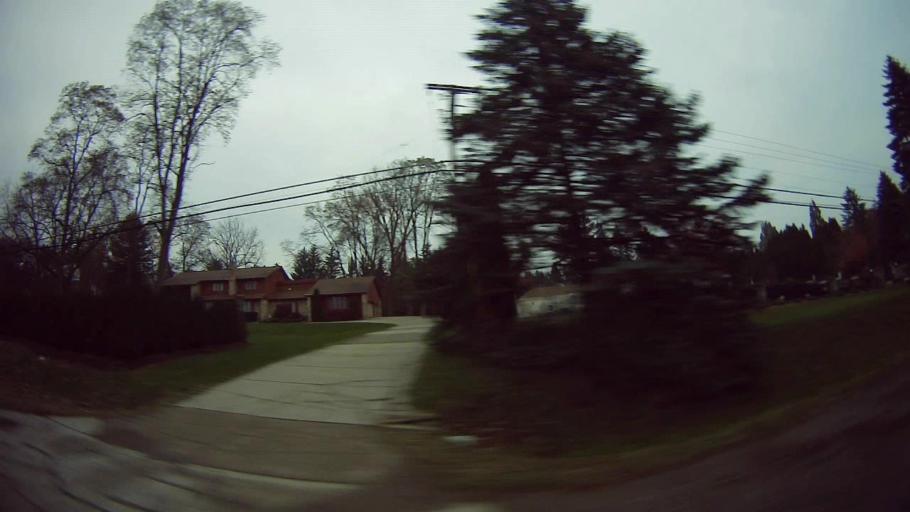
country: US
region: Michigan
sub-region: Oakland County
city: Bloomfield Hills
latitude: 42.5594
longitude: -83.2576
